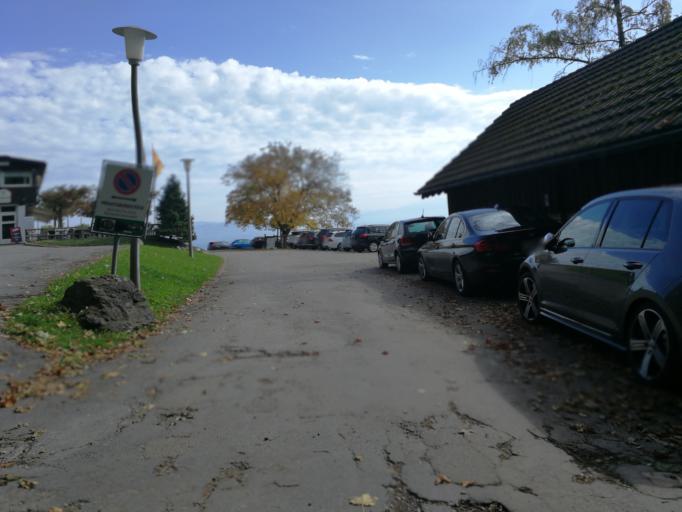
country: CH
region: Zurich
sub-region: Bezirk Uster
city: Egg
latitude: 47.2898
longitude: 8.6749
